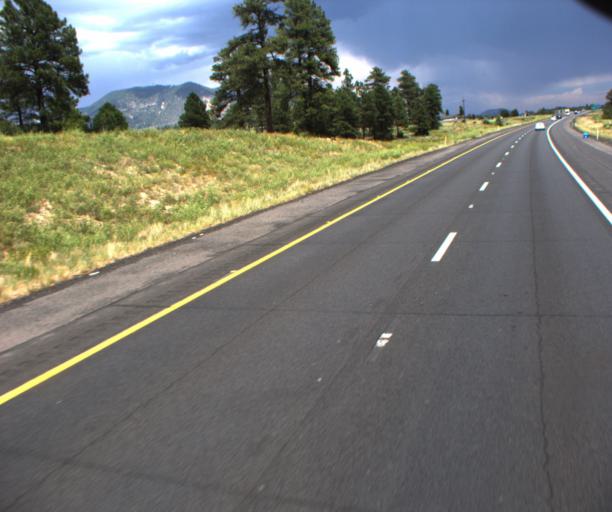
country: US
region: Arizona
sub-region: Coconino County
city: Flagstaff
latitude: 35.1864
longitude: -111.6301
